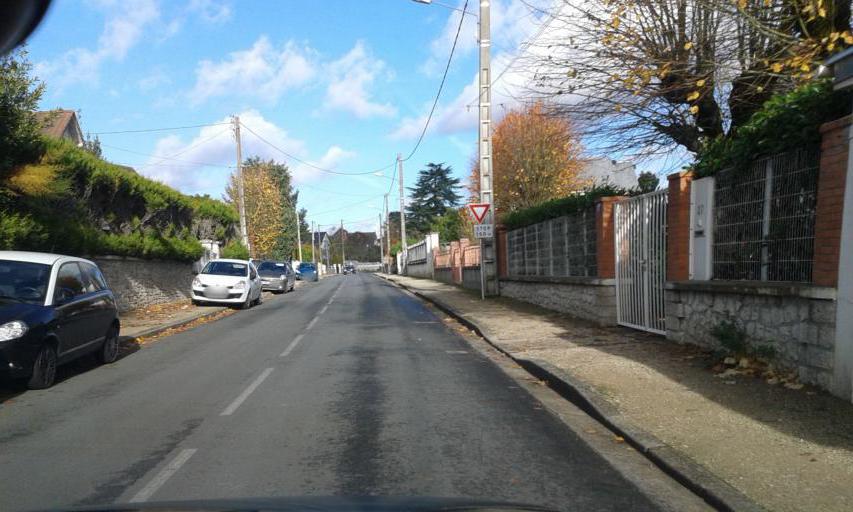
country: FR
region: Centre
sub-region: Departement du Loiret
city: Beaugency
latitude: 47.7701
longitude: 1.6287
